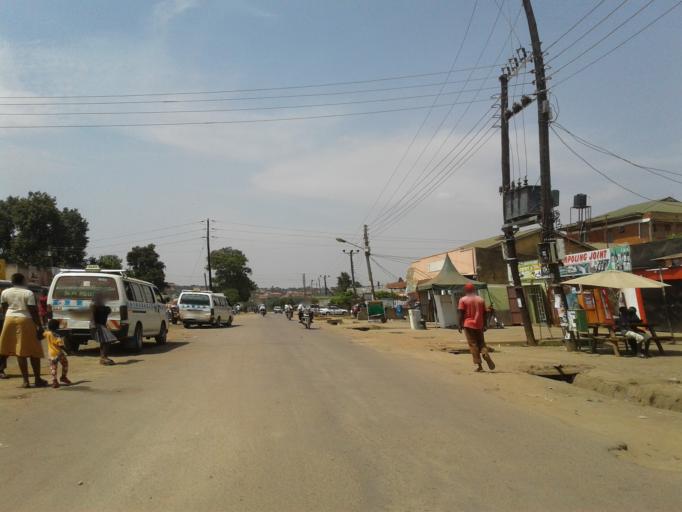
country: UG
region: Central Region
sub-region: Kampala District
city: Kampala
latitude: 0.2552
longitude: 32.6342
